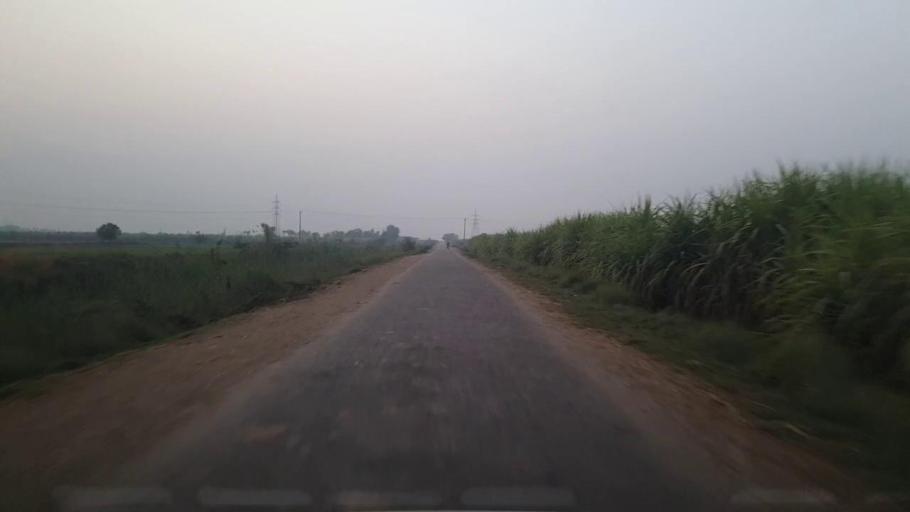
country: PK
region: Sindh
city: Kot Diji
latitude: 27.3408
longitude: 68.6155
